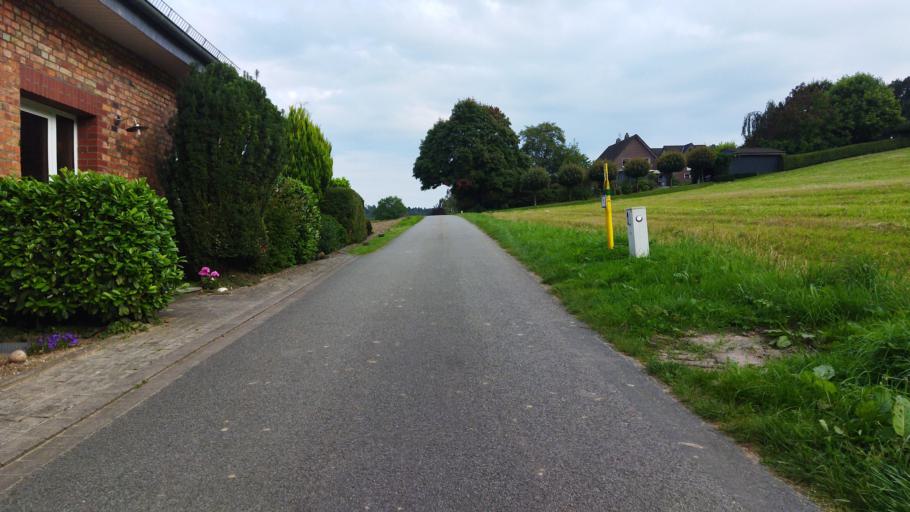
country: DE
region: Lower Saxony
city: Hagen
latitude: 52.1763
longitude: 8.0112
